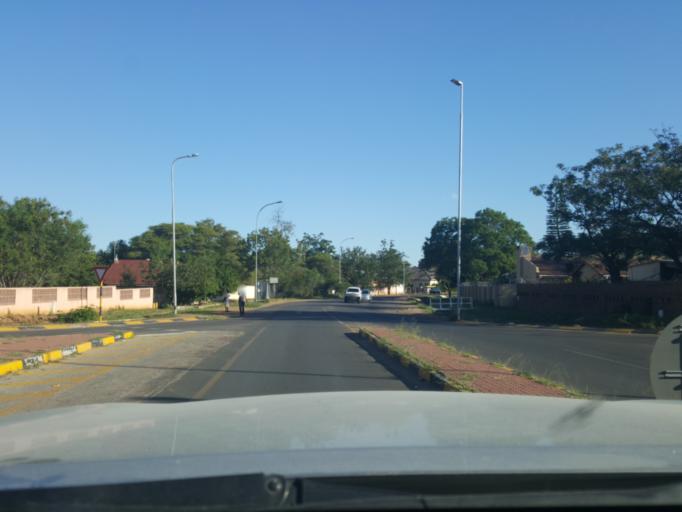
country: BW
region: South East
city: Gaborone
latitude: -24.6265
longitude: 25.9435
